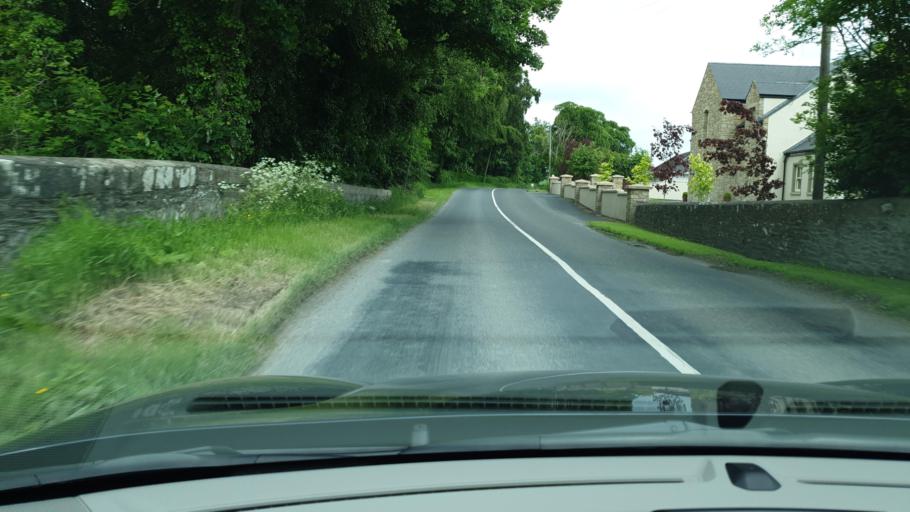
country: IE
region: Leinster
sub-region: An Mhi
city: Slane
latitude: 53.7788
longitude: -6.6321
